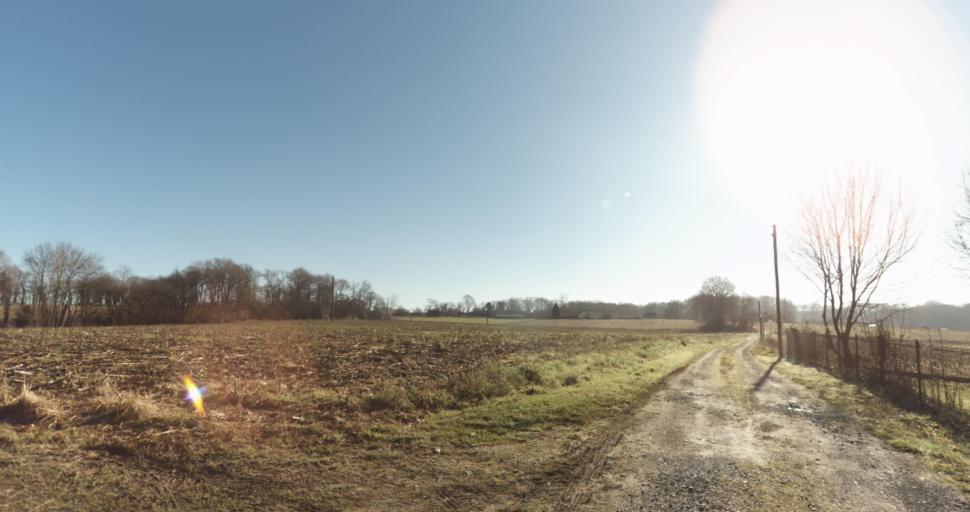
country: FR
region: Aquitaine
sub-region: Departement des Pyrenees-Atlantiques
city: Morlaas
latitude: 43.3462
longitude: -0.2471
